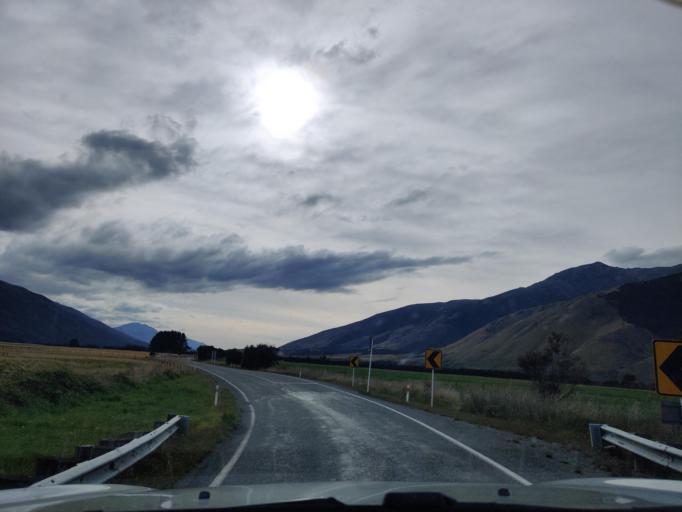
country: NZ
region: Tasman
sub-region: Tasman District
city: Wakefield
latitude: -41.7668
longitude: 172.9691
